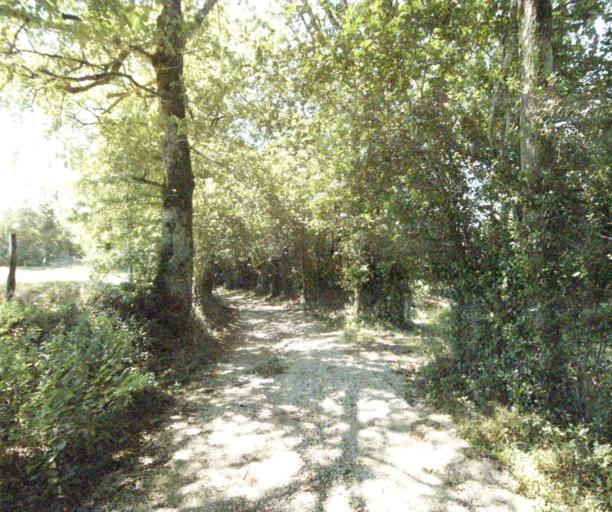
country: FR
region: Midi-Pyrenees
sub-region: Departement du Tarn
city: Dourgne
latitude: 43.4397
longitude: 2.1901
